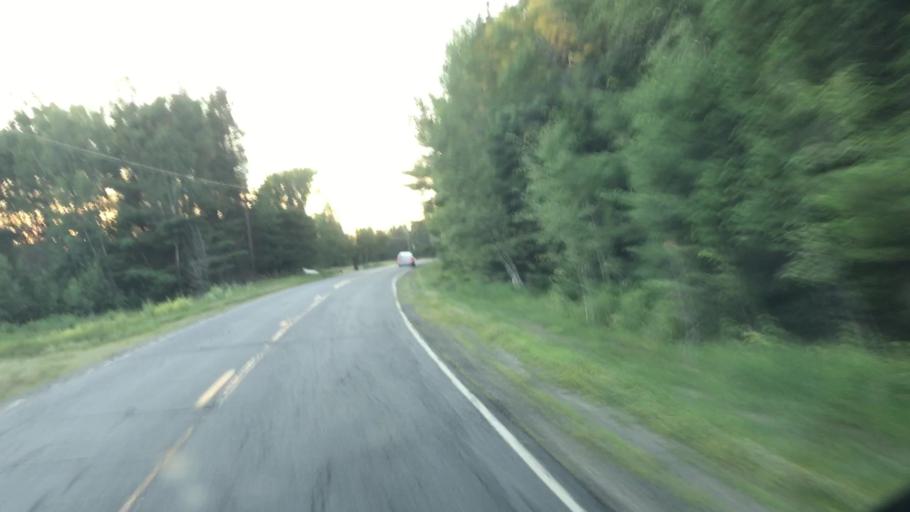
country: US
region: Maine
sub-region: Penobscot County
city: Medway
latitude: 45.5976
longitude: -68.2454
